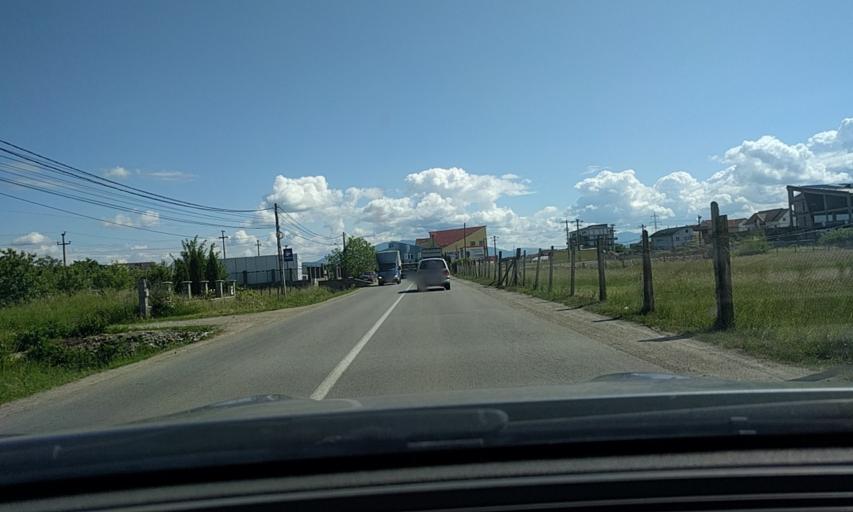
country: RO
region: Bistrita-Nasaud
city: Bistrita
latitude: 47.1537
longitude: 24.5077
